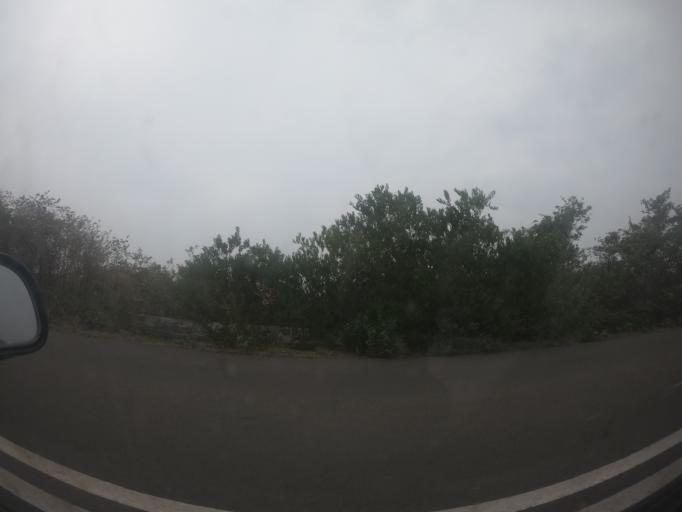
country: AU
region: New South Wales
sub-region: Shellharbour
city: Shellharbour Village
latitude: -34.6058
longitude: 150.8619
